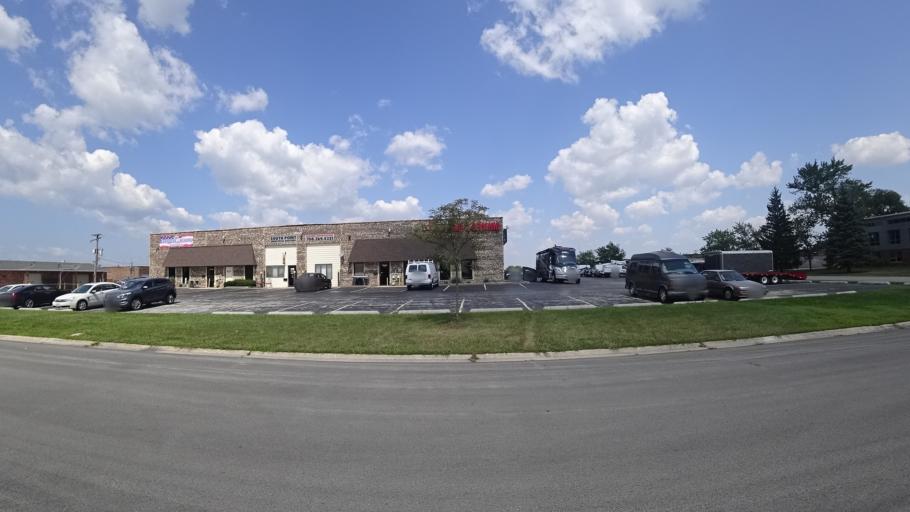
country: US
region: Illinois
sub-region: Cook County
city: Tinley Park
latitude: 41.6059
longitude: -87.7914
